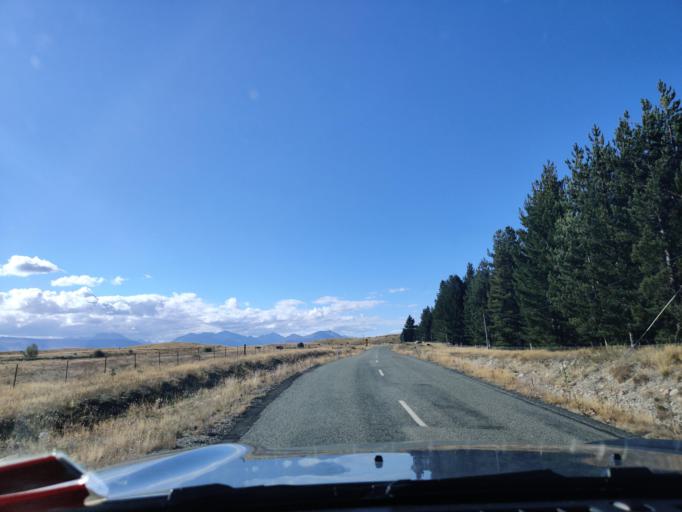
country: NZ
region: Canterbury
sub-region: Timaru District
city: Pleasant Point
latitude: -43.9982
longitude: 170.4506
